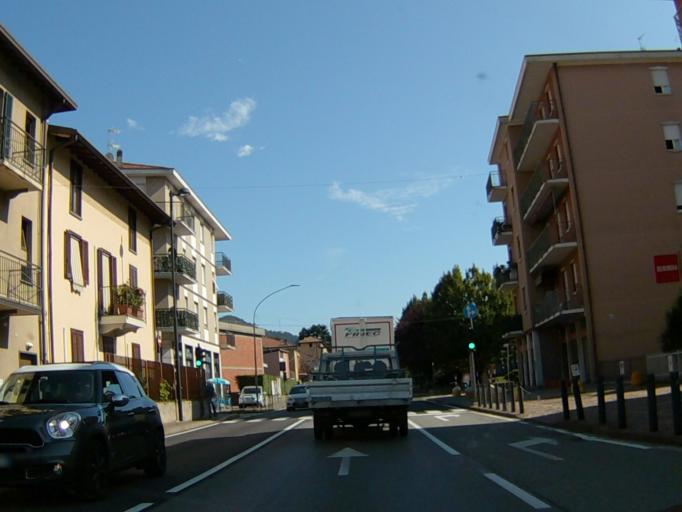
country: IT
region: Lombardy
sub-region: Provincia di Lecco
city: Calolziocorte
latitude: 45.7984
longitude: 9.4335
